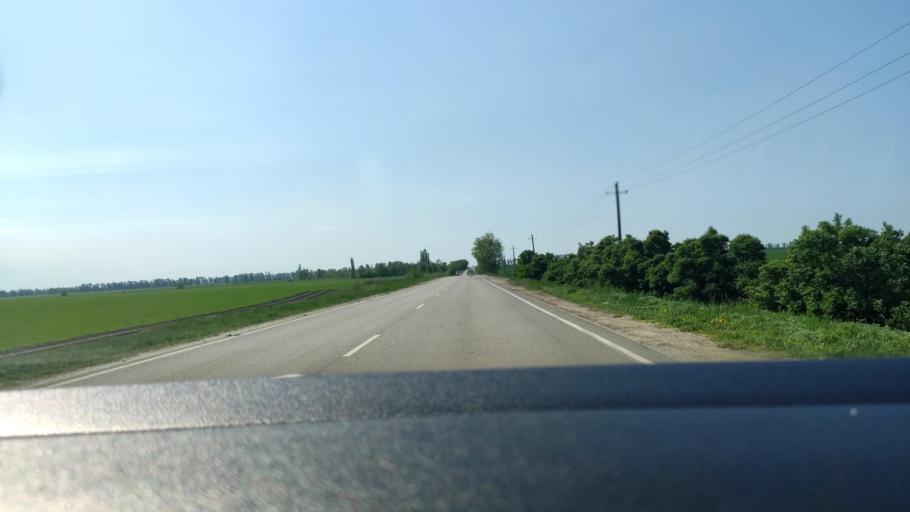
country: RU
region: Voronezj
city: Novaya Usman'
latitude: 51.5788
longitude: 39.3749
